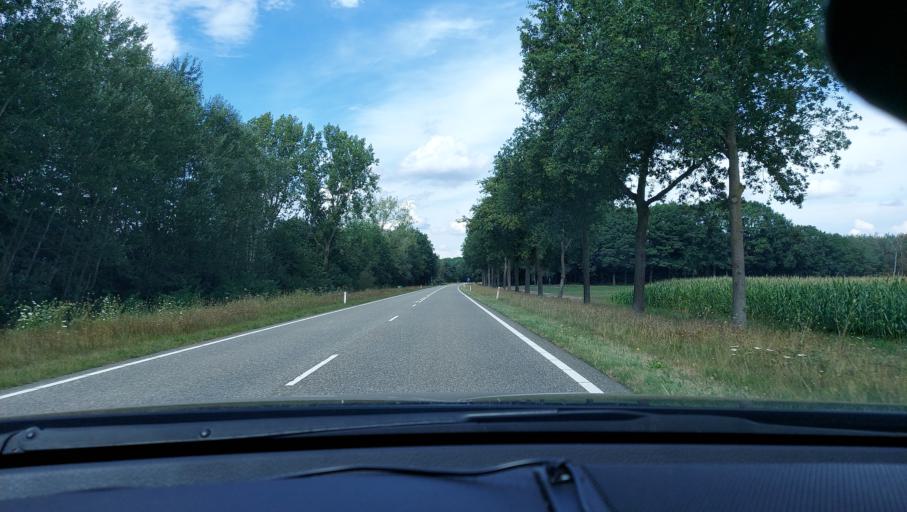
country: NL
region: Limburg
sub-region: Gemeente Beesel
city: Reuver
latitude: 51.3144
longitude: 6.0503
